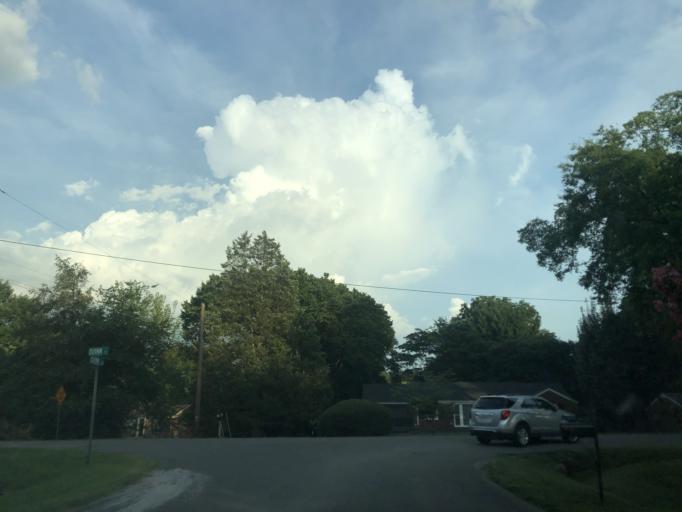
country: US
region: Tennessee
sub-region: Davidson County
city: Nashville
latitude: 36.1584
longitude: -86.7012
